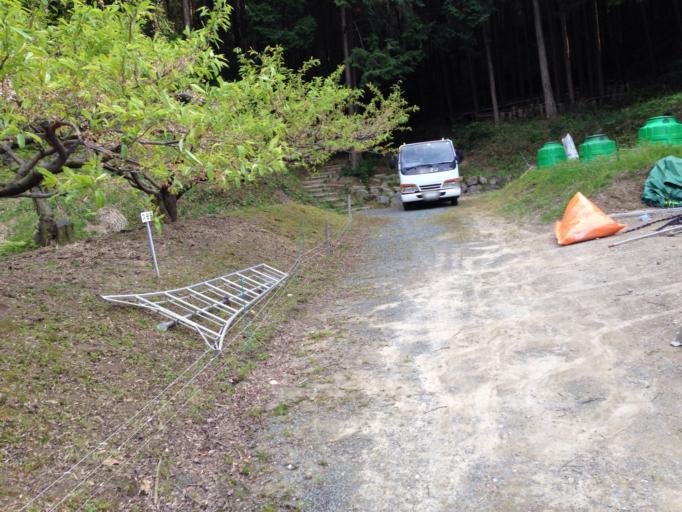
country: JP
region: Shizuoka
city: Kakegawa
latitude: 34.7516
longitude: 137.9998
